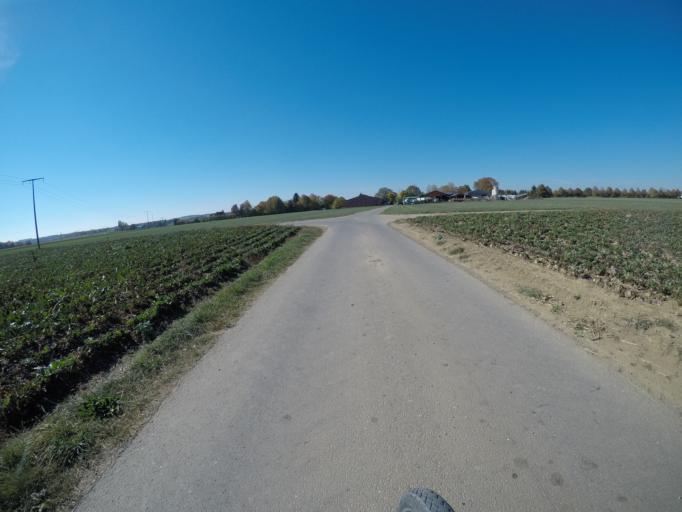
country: DE
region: Baden-Wuerttemberg
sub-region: Regierungsbezirk Stuttgart
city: Bondorf
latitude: 48.5431
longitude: 8.8551
